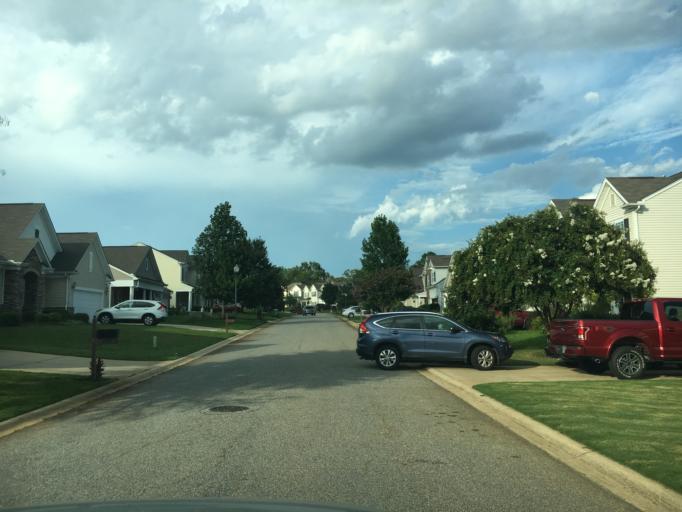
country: US
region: South Carolina
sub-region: Spartanburg County
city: Duncan
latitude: 34.8920
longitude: -82.1284
